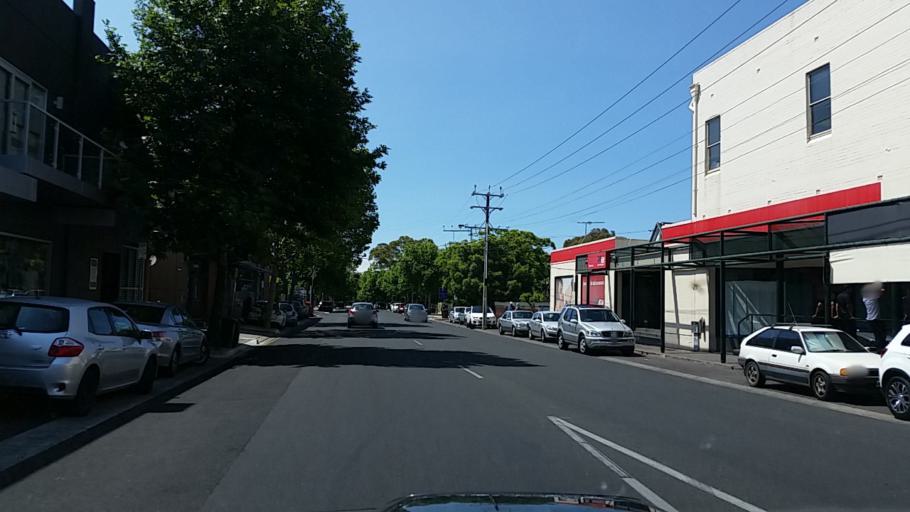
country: AU
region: South Australia
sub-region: Norwood Payneham St Peters
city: Trinity Gardens
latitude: -34.9211
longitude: 138.6344
